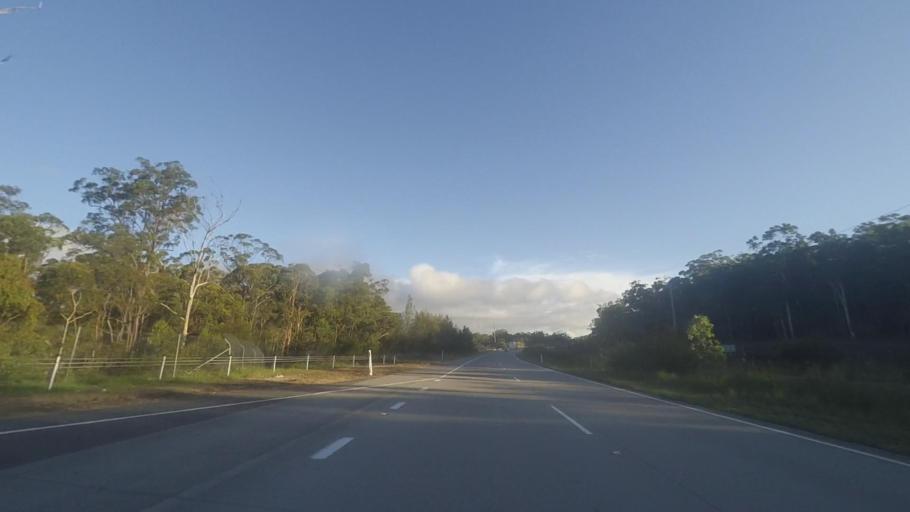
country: AU
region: New South Wales
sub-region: Great Lakes
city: Bulahdelah
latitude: -32.5011
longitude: 152.2099
